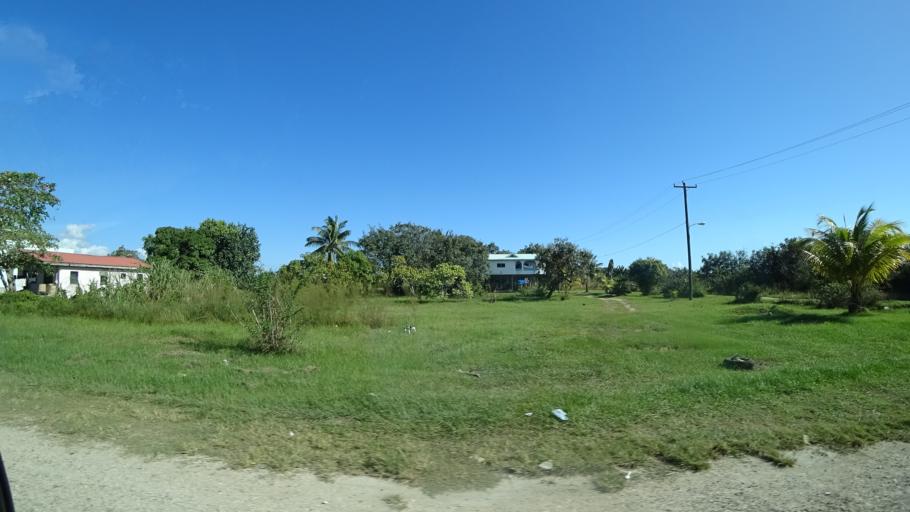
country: BZ
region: Belize
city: Belize City
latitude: 17.5752
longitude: -88.3385
